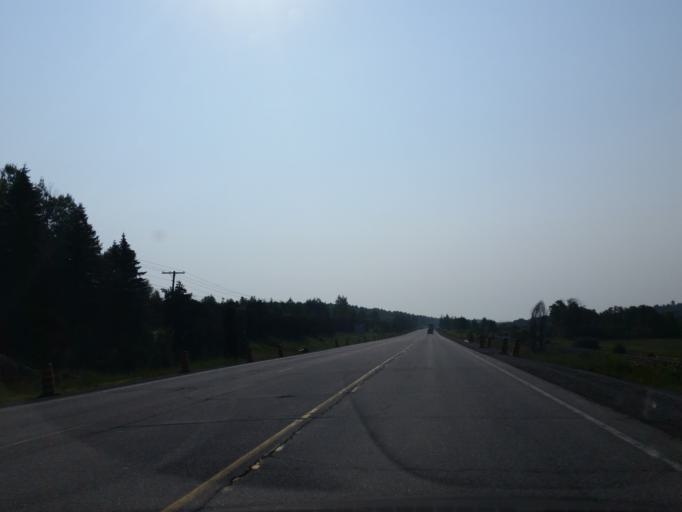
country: CA
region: Ontario
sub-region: Nipissing District
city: North Bay
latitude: 46.4260
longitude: -80.1938
